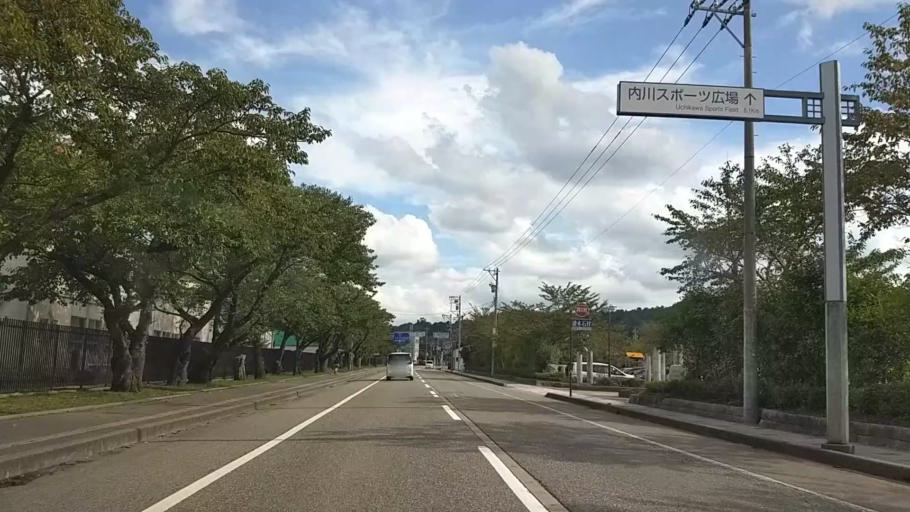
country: JP
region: Ishikawa
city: Nonoichi
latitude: 36.5381
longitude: 136.6663
